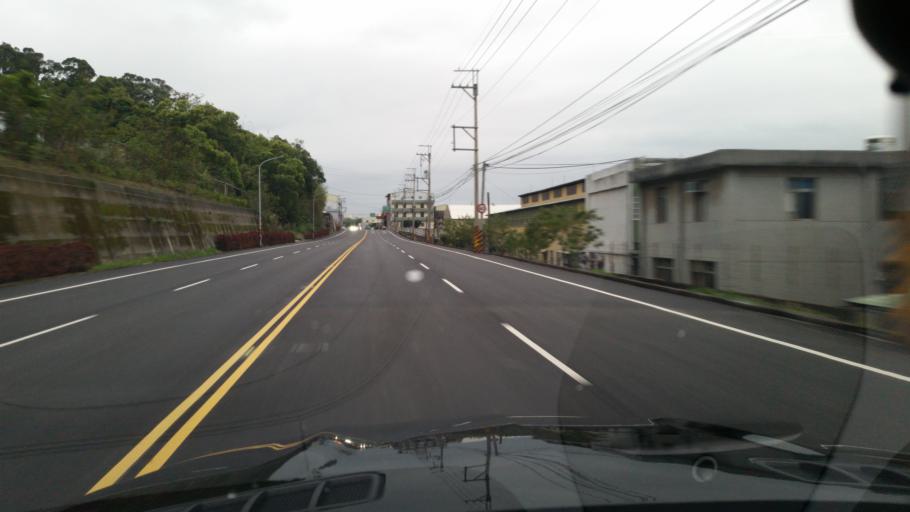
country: TW
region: Taiwan
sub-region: Miaoli
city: Miaoli
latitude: 24.5819
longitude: 120.8737
